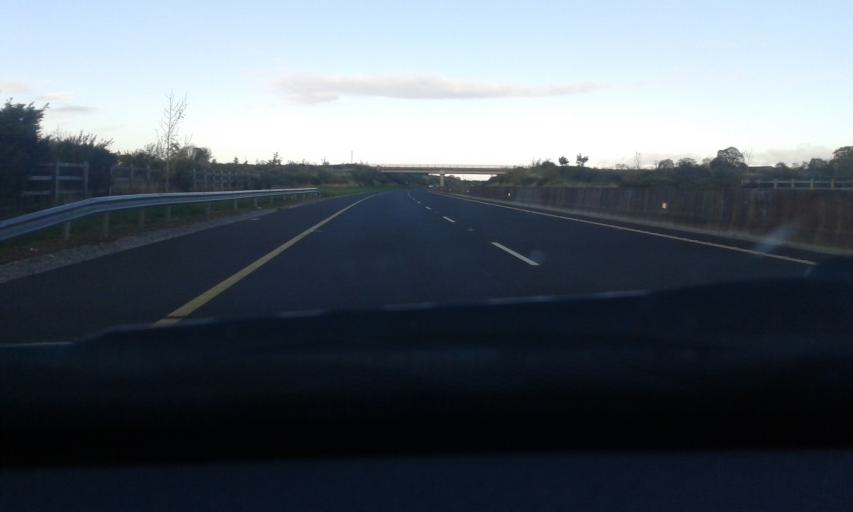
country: IE
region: Munster
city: Thurles
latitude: 52.6471
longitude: -7.7523
